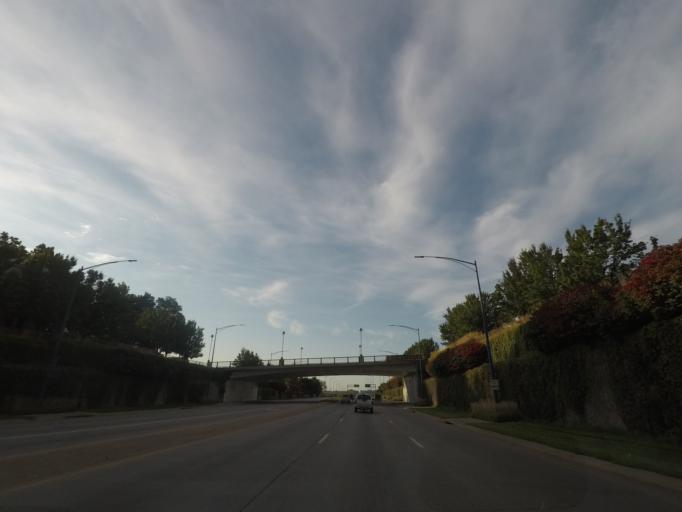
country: US
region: Iowa
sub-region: Polk County
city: Des Moines
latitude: 41.5852
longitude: -93.6449
